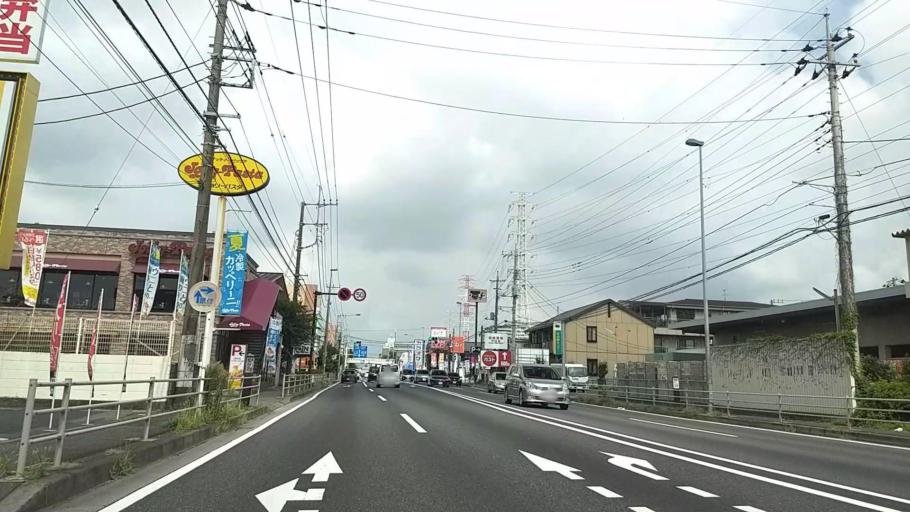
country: JP
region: Tokyo
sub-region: Machida-shi
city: Machida
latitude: 35.5631
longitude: 139.3949
